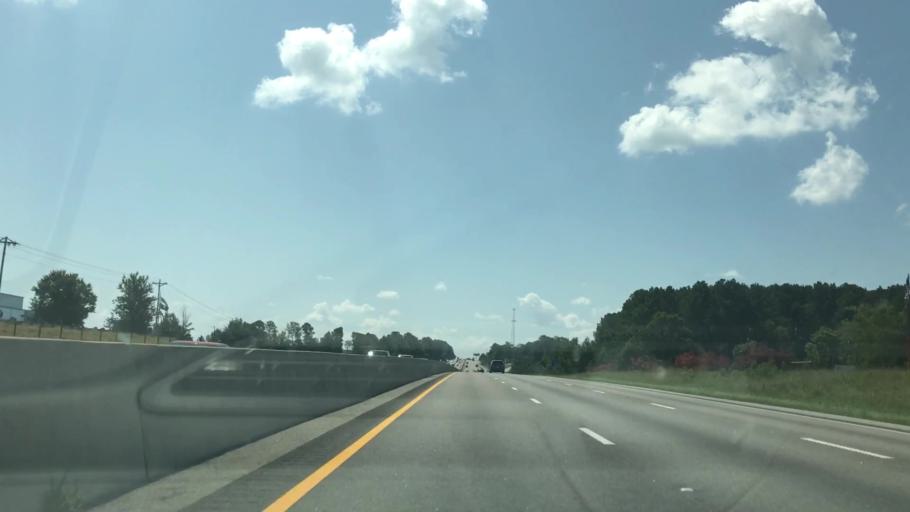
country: US
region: South Carolina
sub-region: Lexington County
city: Gaston
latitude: 33.8456
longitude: -81.0237
